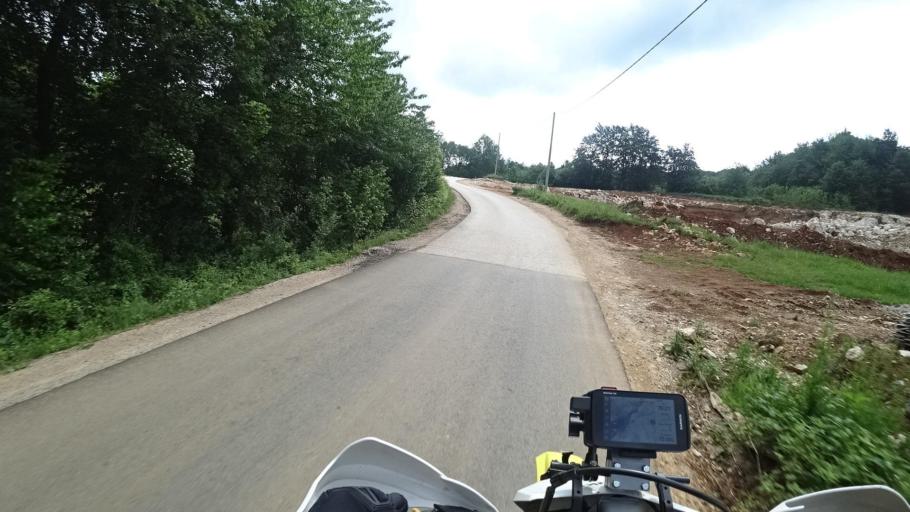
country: HR
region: Licko-Senjska
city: Jezerce
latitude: 44.9342
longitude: 15.6315
